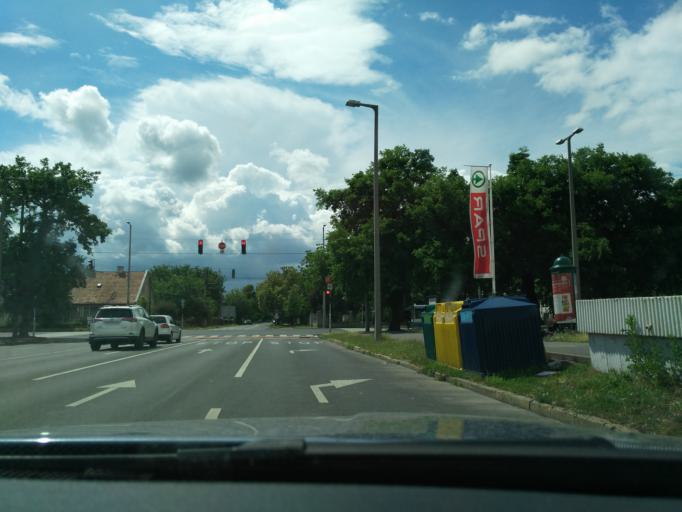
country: HU
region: Hajdu-Bihar
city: Debrecen
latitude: 47.5476
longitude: 21.6105
